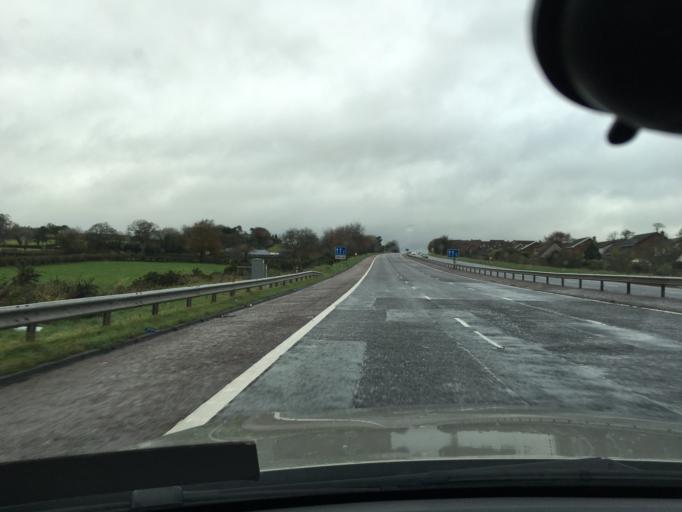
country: GB
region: Northern Ireland
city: Carnmoney
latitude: 54.6819
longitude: -5.9770
